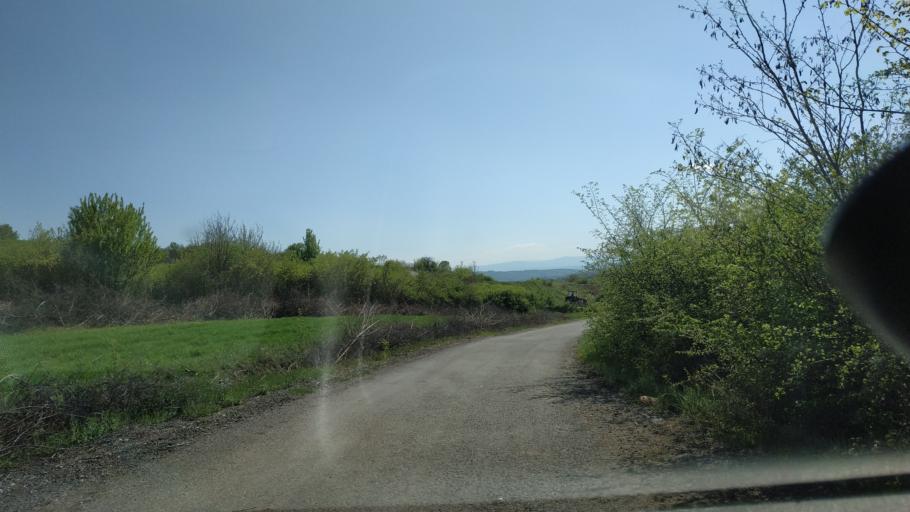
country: RS
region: Central Serbia
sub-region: Zajecarski Okrug
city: Soko Banja
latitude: 43.4915
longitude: 21.8730
